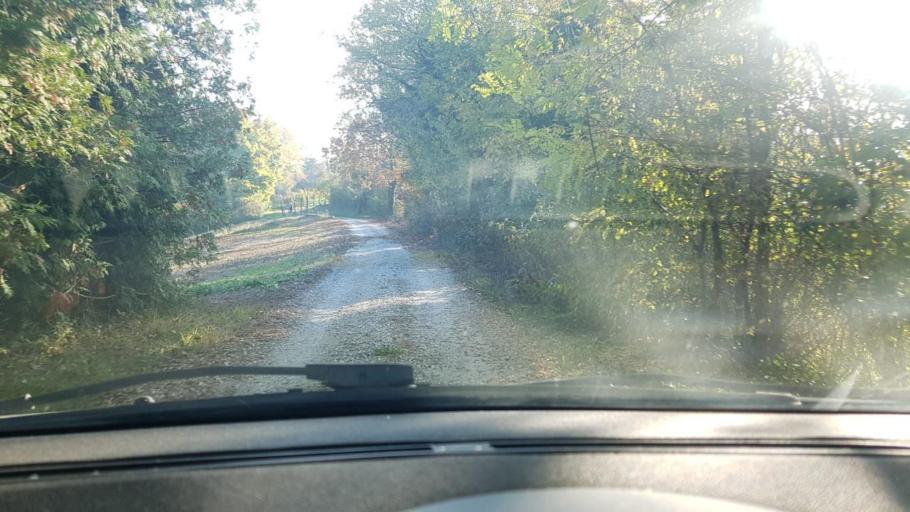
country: HR
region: Krapinsko-Zagorska
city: Zabok
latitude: 46.0341
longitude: 15.8867
